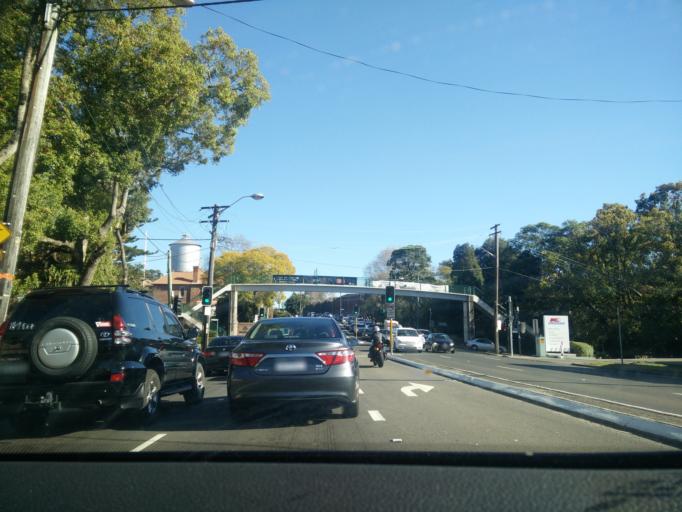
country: AU
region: New South Wales
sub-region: Ku-ring-gai
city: North Wahroonga
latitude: -33.7199
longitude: 151.1163
